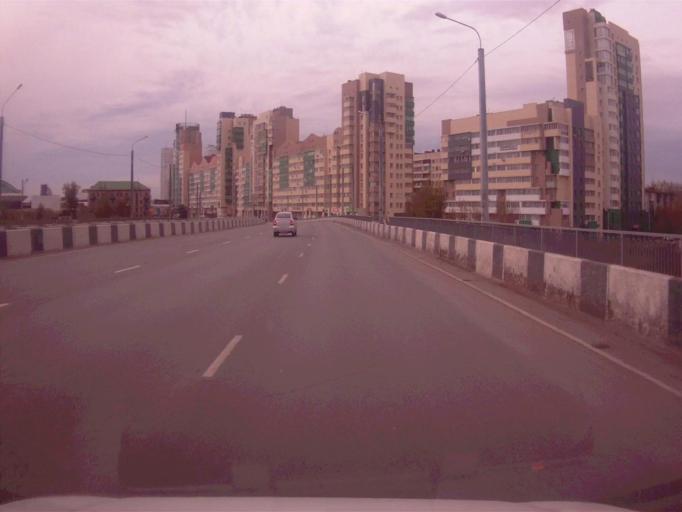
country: RU
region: Chelyabinsk
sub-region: Gorod Chelyabinsk
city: Chelyabinsk
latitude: 55.1732
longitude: 61.4078
